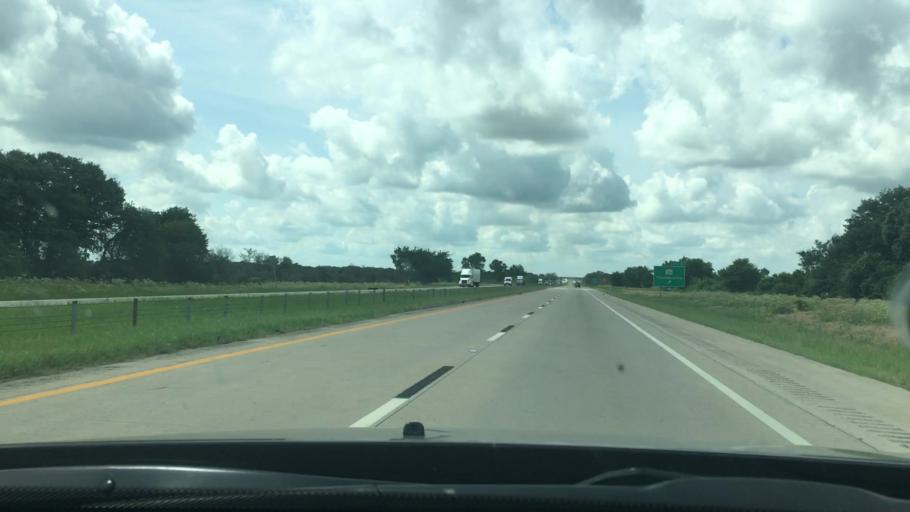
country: US
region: Oklahoma
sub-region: Love County
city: Marietta
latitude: 33.8018
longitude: -97.1351
